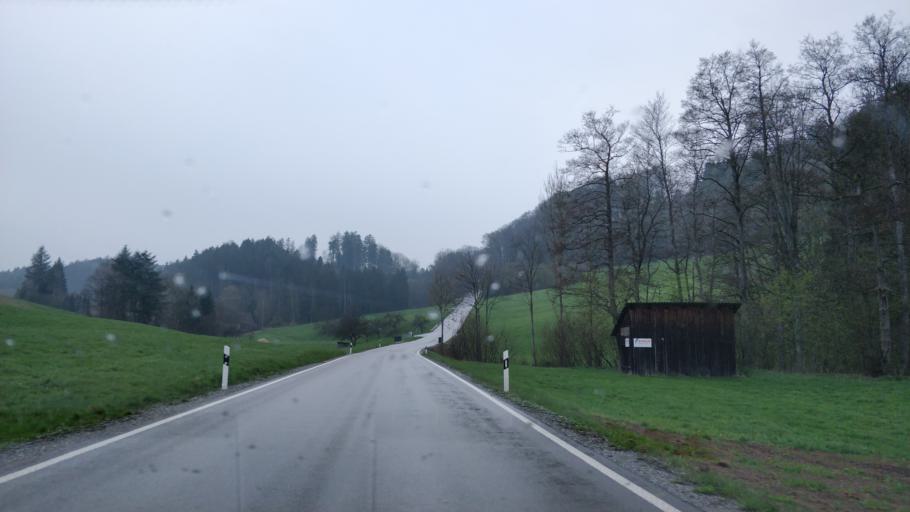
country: DE
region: Baden-Wuerttemberg
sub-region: Regierungsbezirk Stuttgart
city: Oberrot
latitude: 49.0362
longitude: 9.6216
